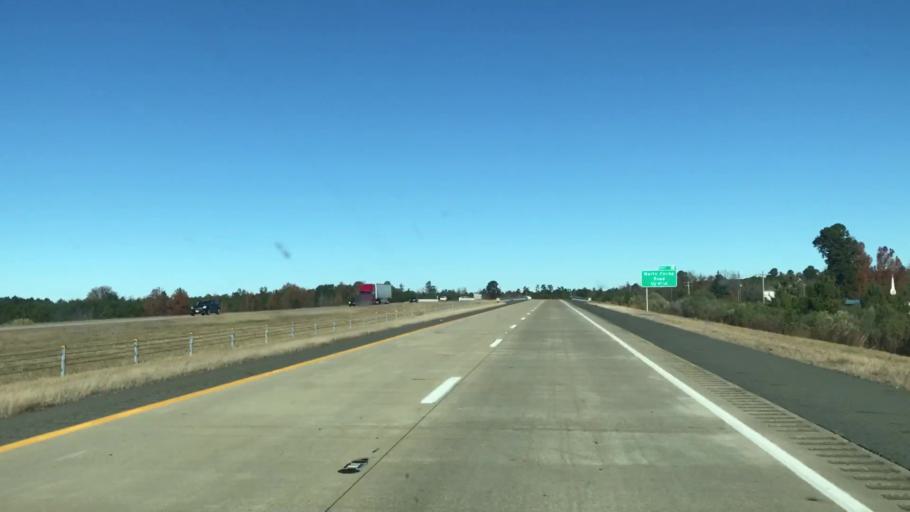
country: US
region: Texas
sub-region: Bowie County
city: Texarkana
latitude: 33.2563
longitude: -93.8945
